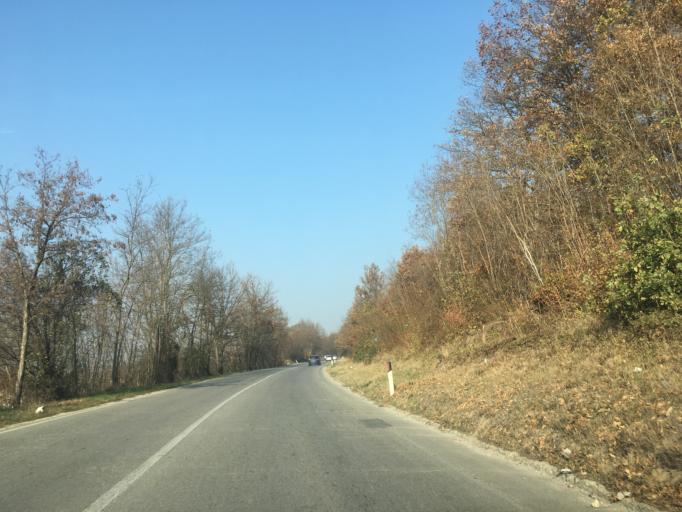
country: XK
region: Pec
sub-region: Komuna e Pejes
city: Dubova (Driloni)
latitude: 42.6447
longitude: 20.4133
